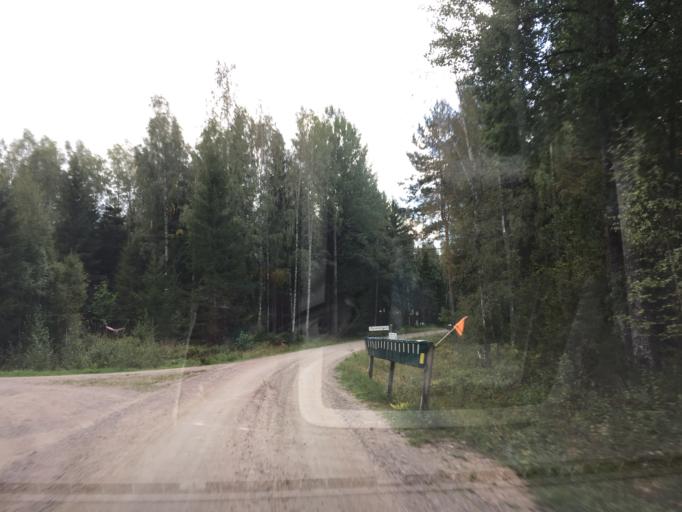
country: SE
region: Soedermanland
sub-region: Vingakers Kommun
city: Vingaker
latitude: 58.9955
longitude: 15.7398
